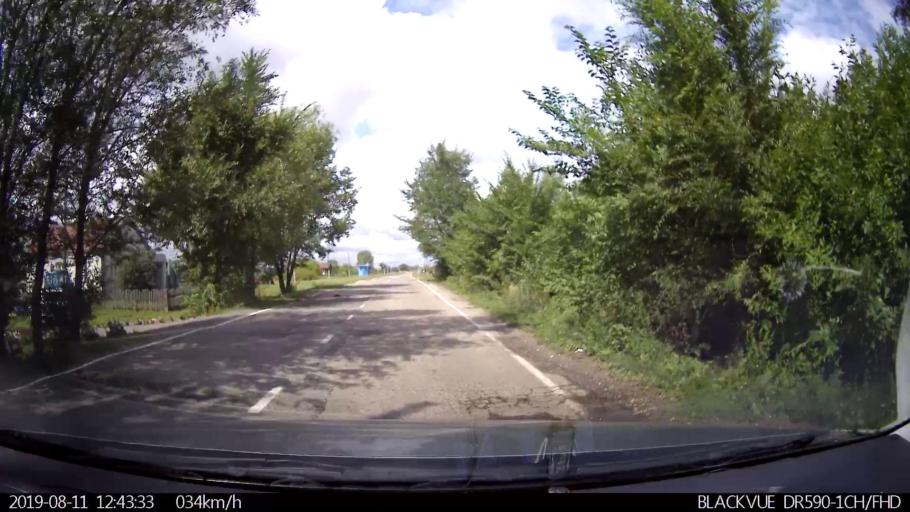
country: RU
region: Ulyanovsk
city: Ignatovka
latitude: 53.8512
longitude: 47.7422
